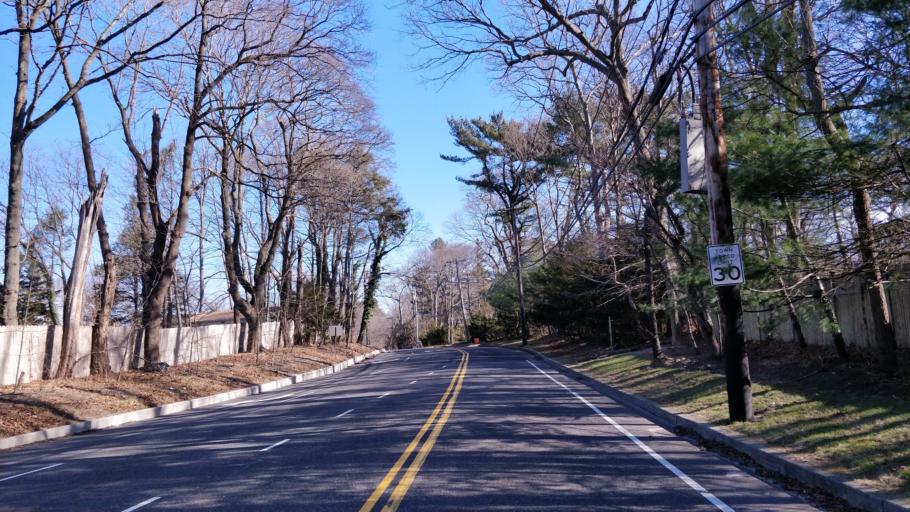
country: US
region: New York
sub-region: Suffolk County
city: Smithtown
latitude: 40.8617
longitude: -73.1963
